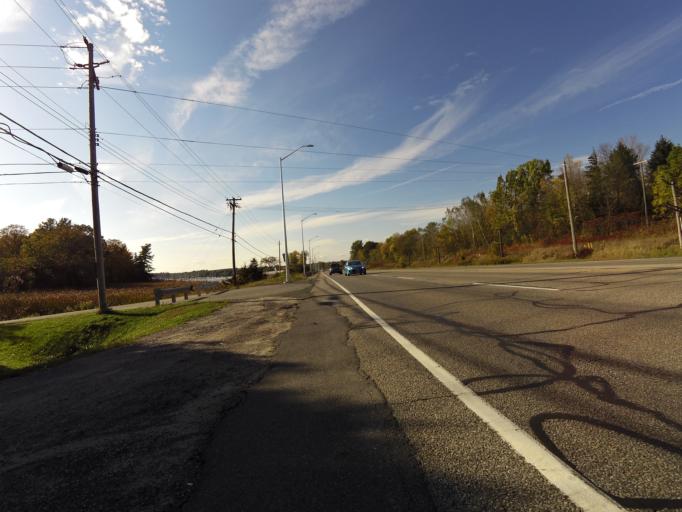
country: CA
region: Ontario
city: Kingston
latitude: 44.2392
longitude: -76.5947
